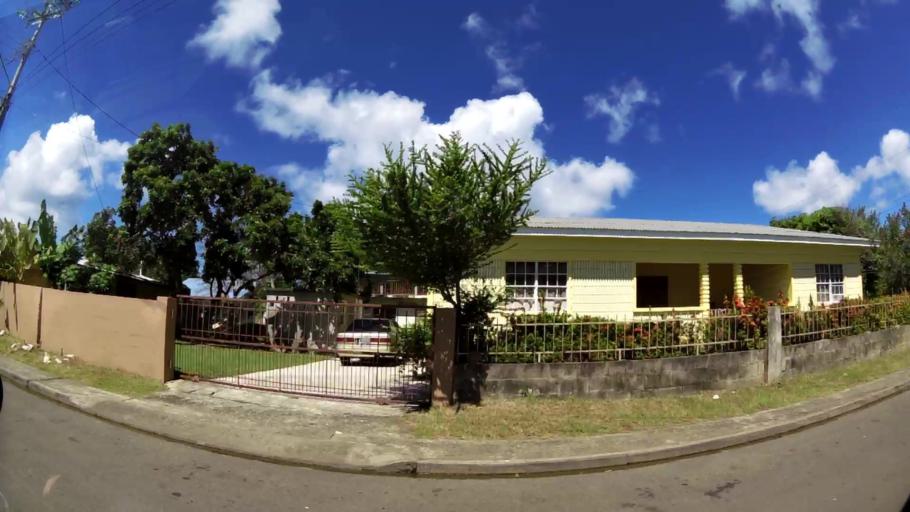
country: TT
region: Tobago
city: Scarborough
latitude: 11.1820
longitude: -60.8054
